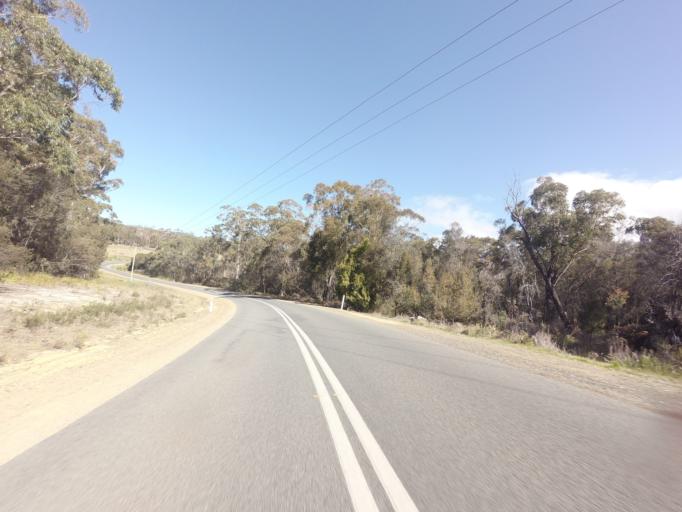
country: AU
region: Tasmania
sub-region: Break O'Day
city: St Helens
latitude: -41.6893
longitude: 148.2799
